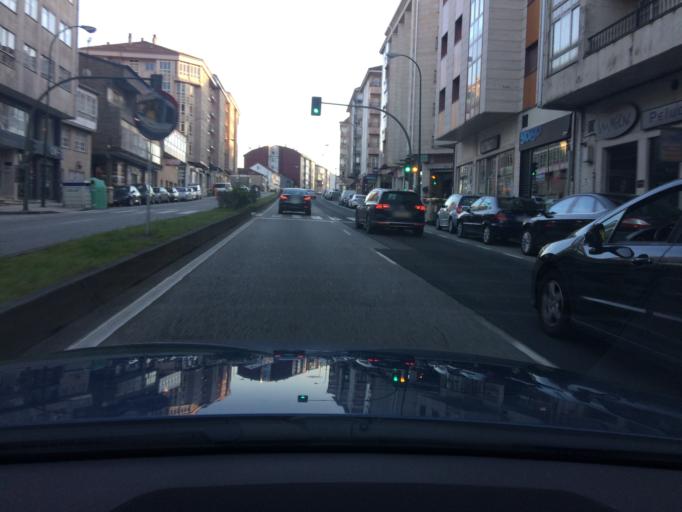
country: ES
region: Galicia
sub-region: Provincia da Coruna
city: Santiago de Compostela
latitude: 42.8441
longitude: -8.5770
